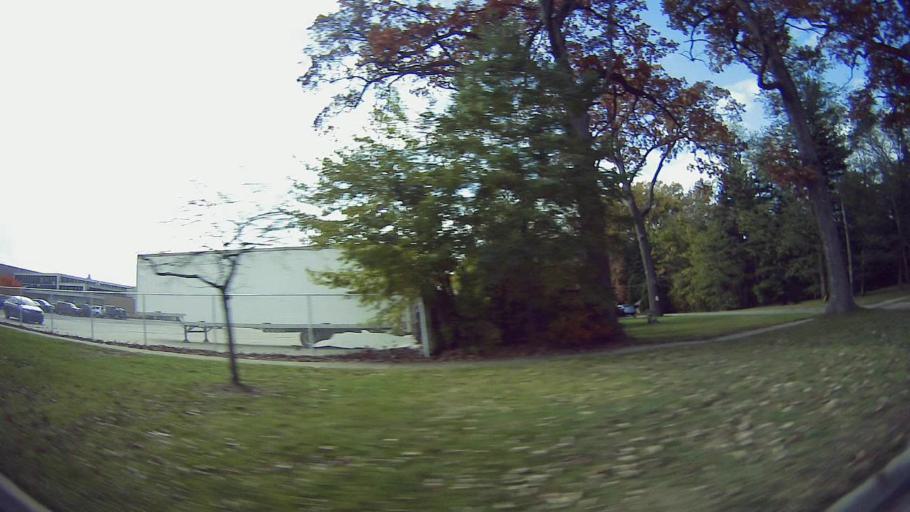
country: US
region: Michigan
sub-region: Macomb County
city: Warren
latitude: 42.4806
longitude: -83.0661
